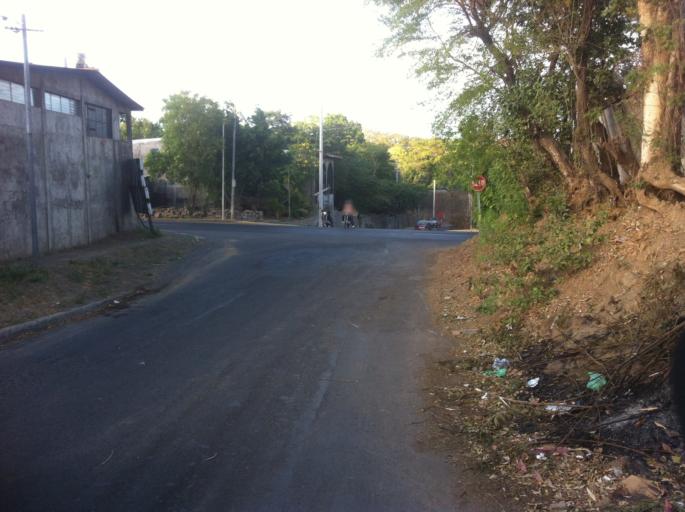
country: NI
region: Managua
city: Managua
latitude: 12.1077
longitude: -86.2999
